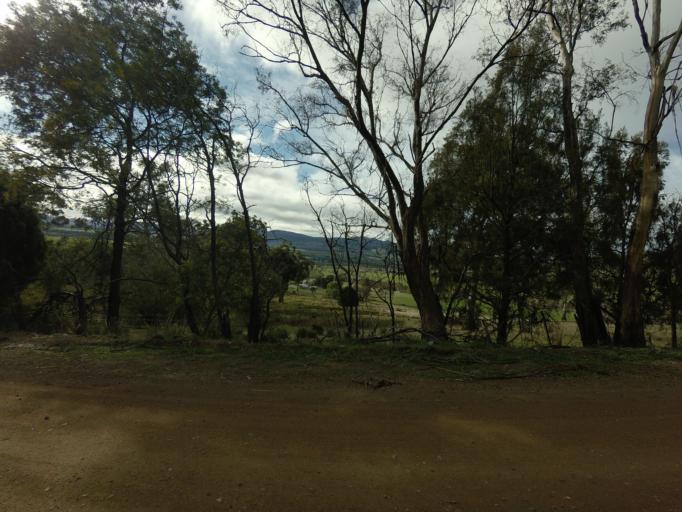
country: AU
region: Tasmania
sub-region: Derwent Valley
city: New Norfolk
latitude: -42.7246
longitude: 146.8718
